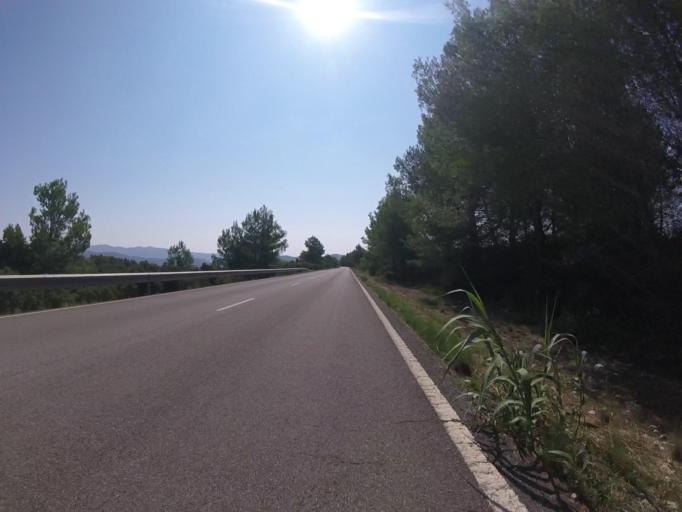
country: ES
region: Valencia
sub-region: Provincia de Castello
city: Benafigos
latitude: 40.2454
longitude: -0.1963
